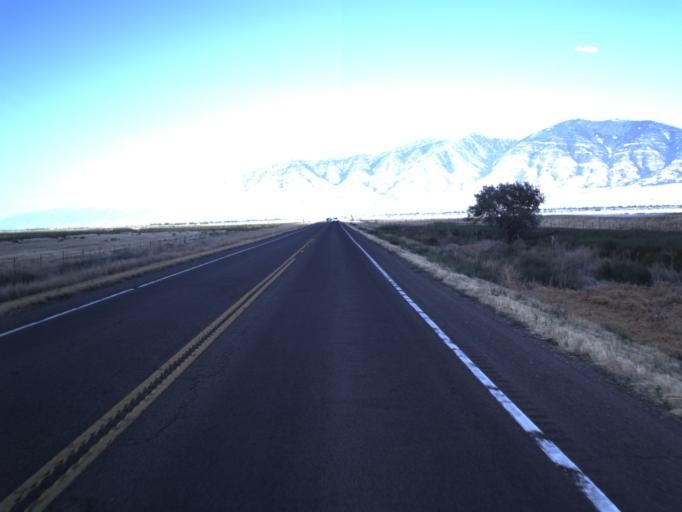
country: US
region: Utah
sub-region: Tooele County
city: Erda
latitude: 40.6165
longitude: -112.3670
